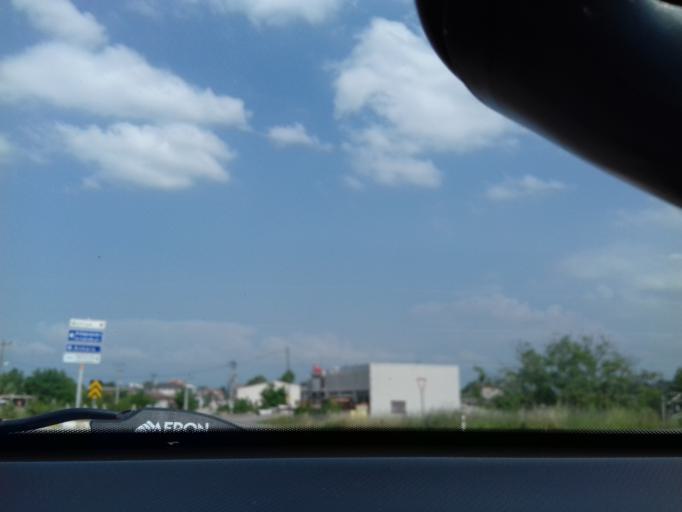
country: TR
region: Sakarya
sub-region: Merkez
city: Sapanca
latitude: 40.7135
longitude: 30.3456
